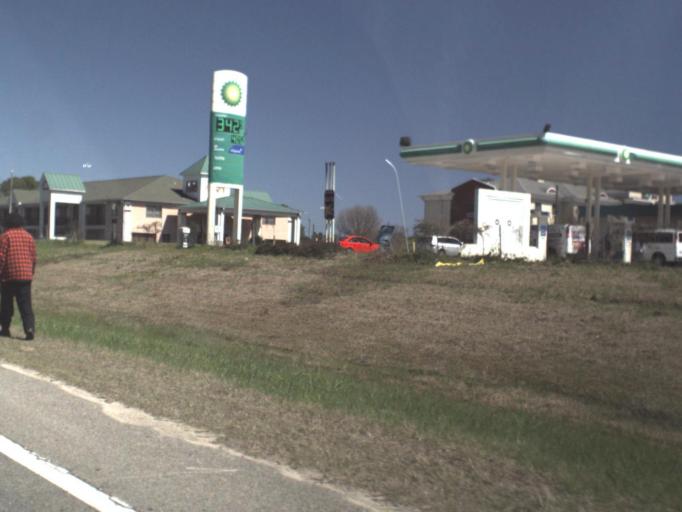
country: US
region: Florida
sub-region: Gadsden County
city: Quincy
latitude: 30.5353
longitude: -84.5963
